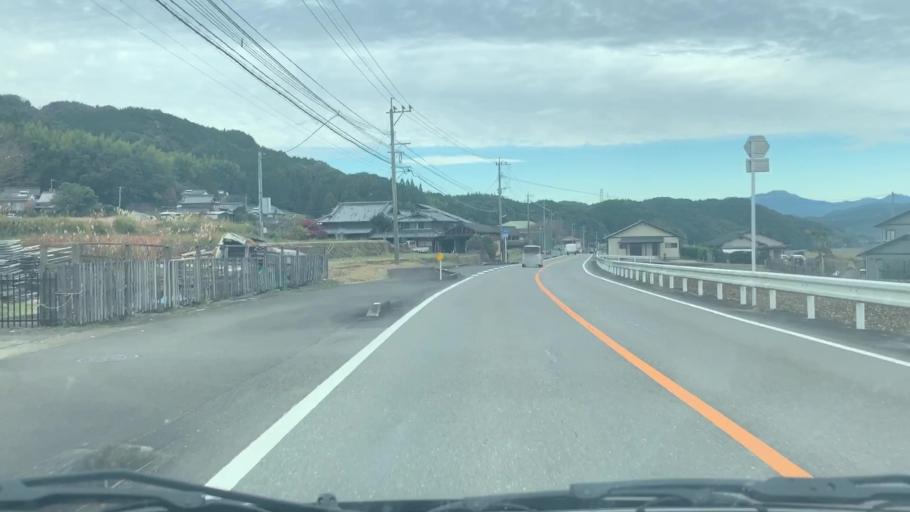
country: JP
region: Saga Prefecture
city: Takeocho-takeo
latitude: 33.1714
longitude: 129.9693
